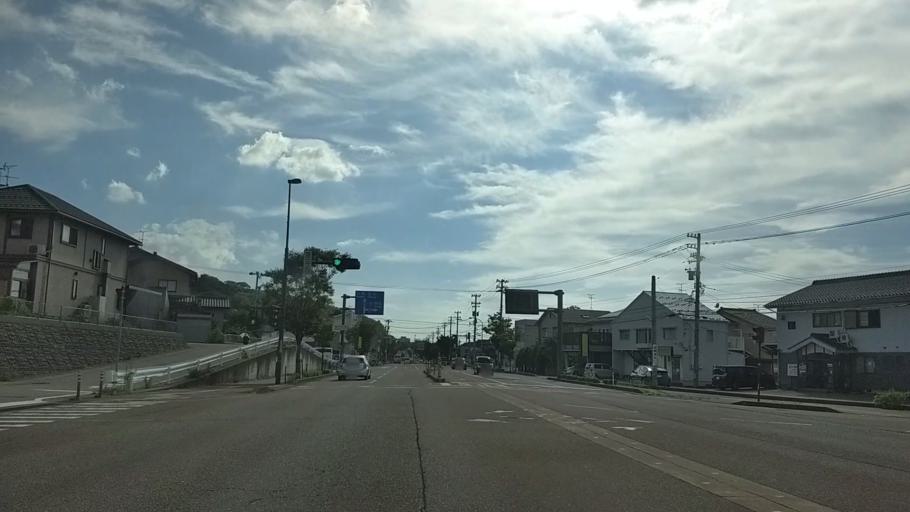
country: JP
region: Ishikawa
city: Nonoichi
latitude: 36.5242
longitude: 136.6426
